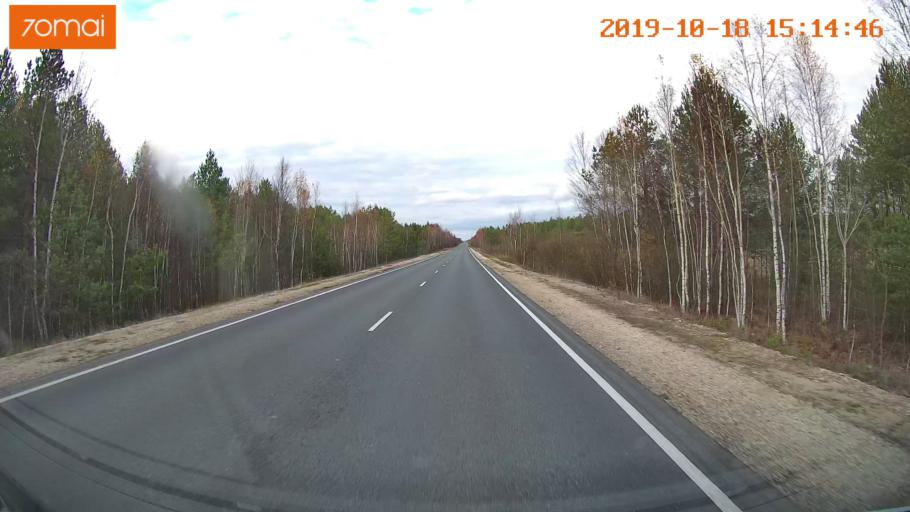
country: RU
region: Vladimir
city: Gus'-Khrustal'nyy
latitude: 55.6080
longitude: 40.7211
